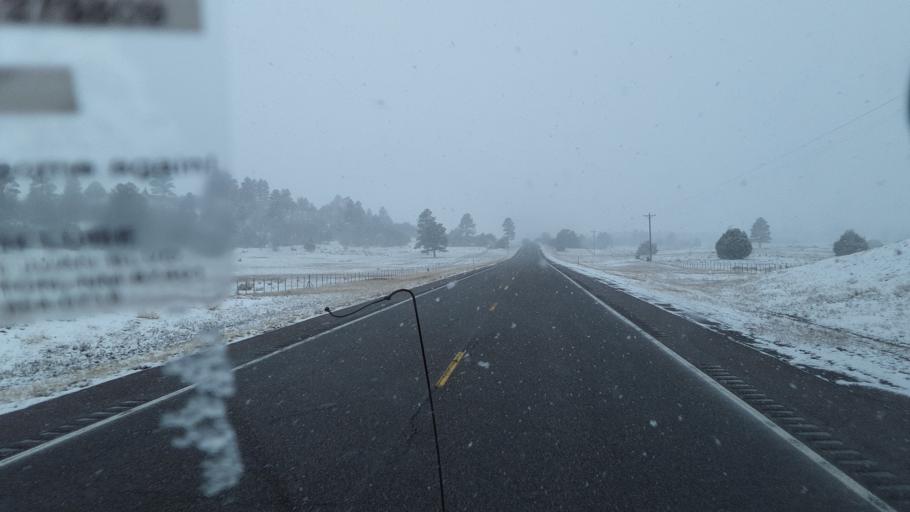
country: US
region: New Mexico
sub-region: Rio Arriba County
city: Chama
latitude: 36.8793
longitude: -106.6938
